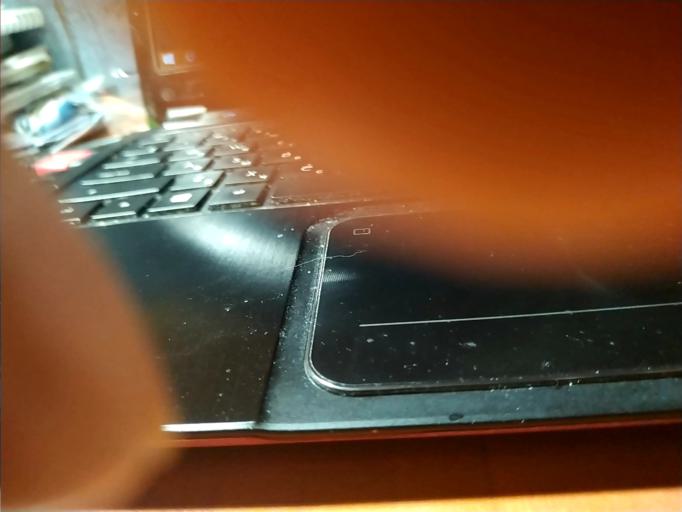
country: RU
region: Tverskaya
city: Ves'yegonsk
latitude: 58.7032
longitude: 37.5439
